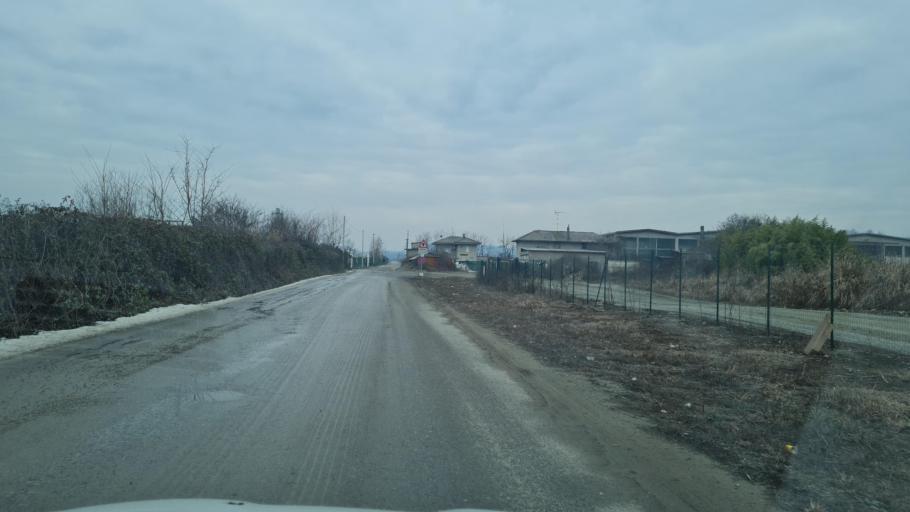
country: IT
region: Piedmont
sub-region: Provincia di Biella
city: Cavaglia
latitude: 45.3818
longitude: 8.1117
